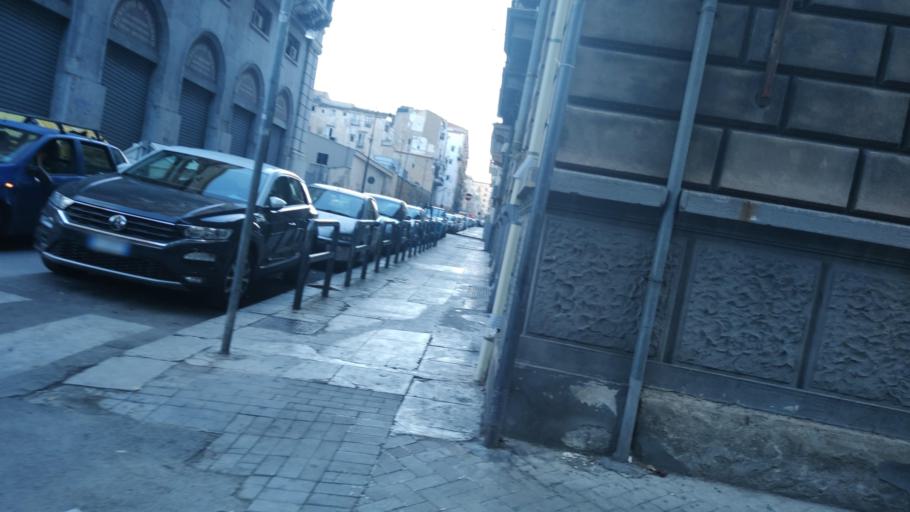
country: IT
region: Sicily
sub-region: Palermo
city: Palermo
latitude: 38.1112
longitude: 13.3661
